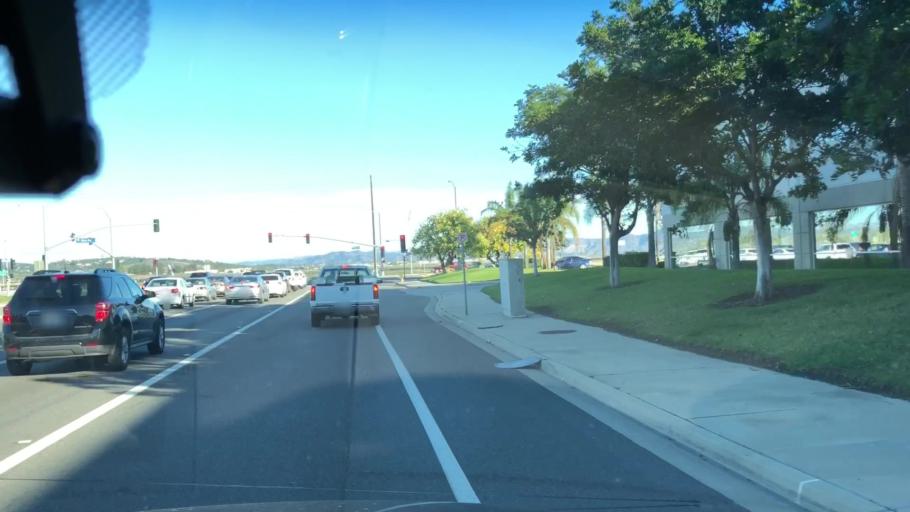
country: US
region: California
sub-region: Ventura County
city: El Rio
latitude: 34.2187
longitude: -119.1433
